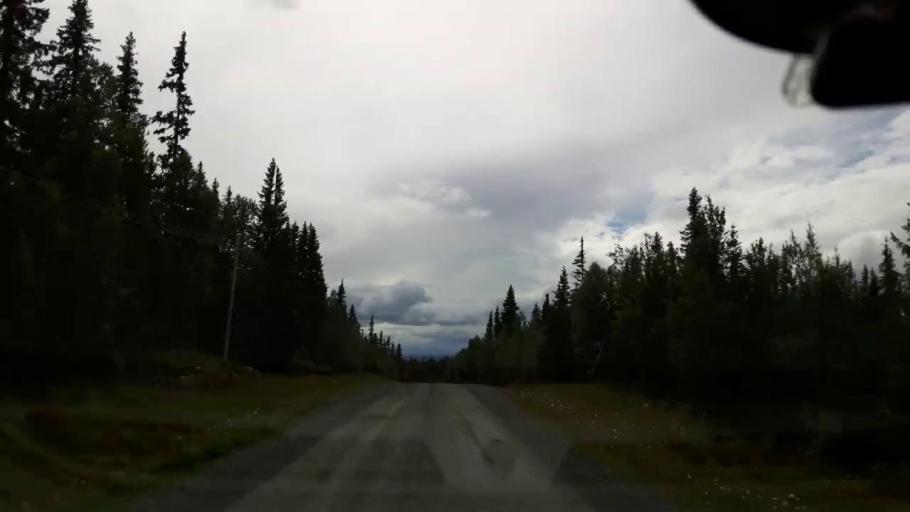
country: SE
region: Jaemtland
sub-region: Krokoms Kommun
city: Valla
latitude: 63.7623
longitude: 13.8374
